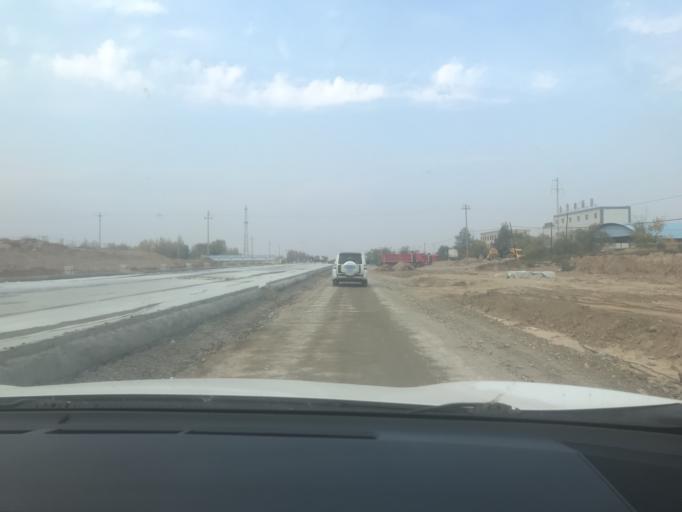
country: CN
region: Gansu Sheng
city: Gulang
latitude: 37.5133
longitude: 102.9010
